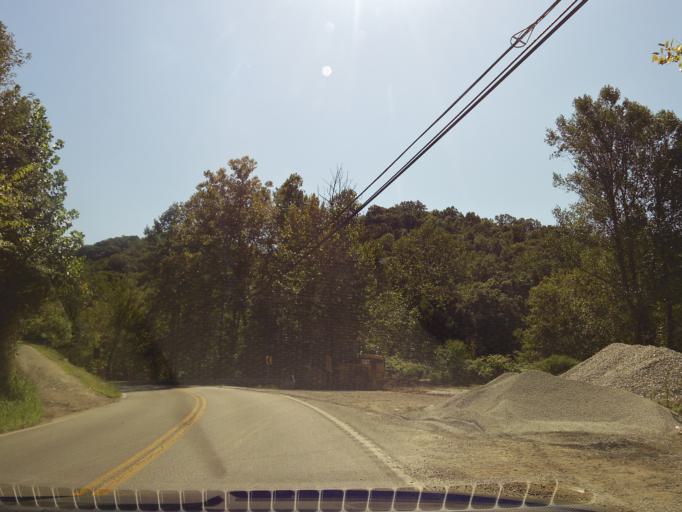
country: US
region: Kentucky
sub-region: Clay County
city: Manchester
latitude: 37.0859
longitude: -83.6907
